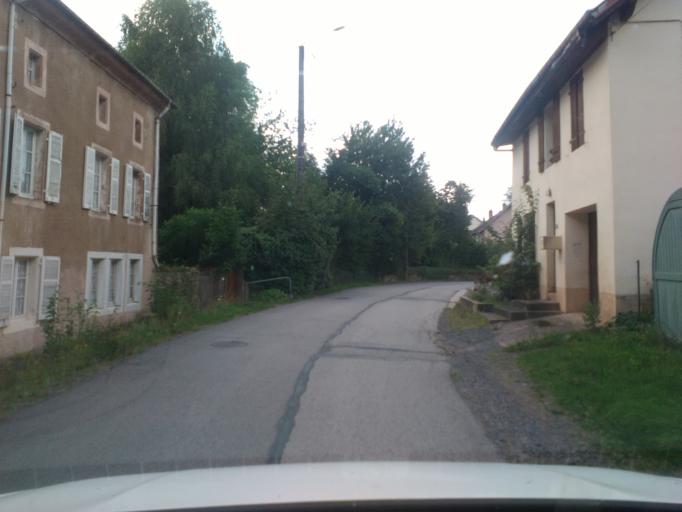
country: FR
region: Lorraine
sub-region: Departement des Vosges
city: Senones
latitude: 48.4354
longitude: 7.0304
